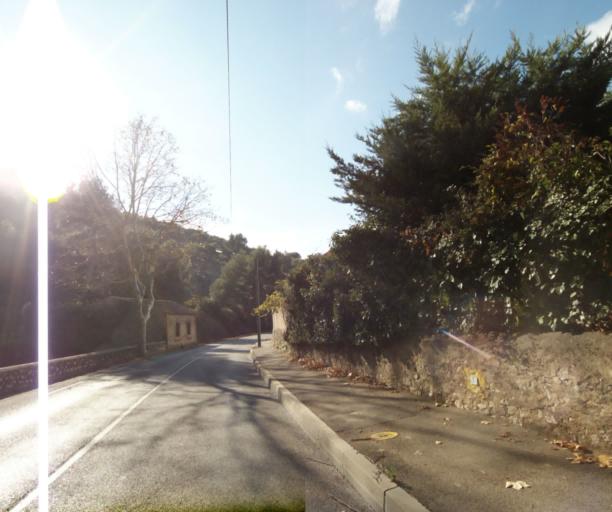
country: FR
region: Provence-Alpes-Cote d'Azur
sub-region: Departement des Bouches-du-Rhone
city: Allauch
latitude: 43.3598
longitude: 5.4940
